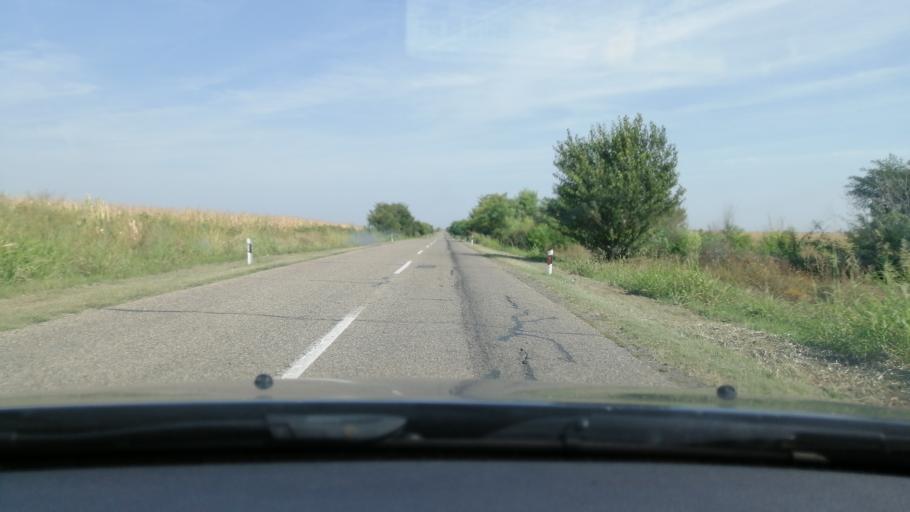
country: RS
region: Autonomna Pokrajina Vojvodina
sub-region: Juznobanatski Okrug
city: Kovacica
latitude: 45.1384
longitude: 20.6163
